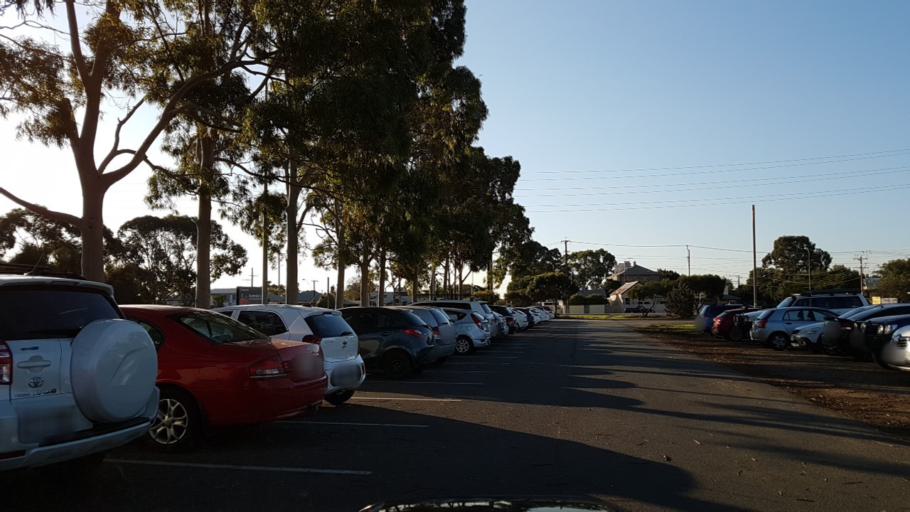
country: AU
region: South Australia
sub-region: Port Adelaide Enfield
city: Birkenhead
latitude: -34.8418
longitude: 138.4937
